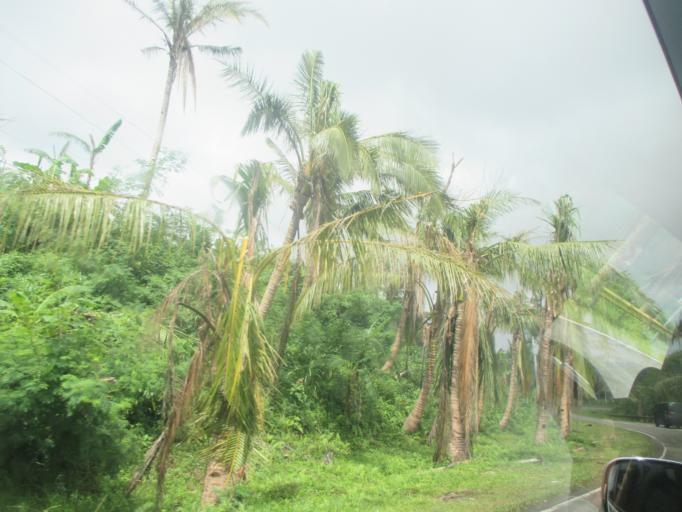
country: PH
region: Eastern Visayas
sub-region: Province of Samar
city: Calbiga
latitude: 11.5509
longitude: 125.0173
